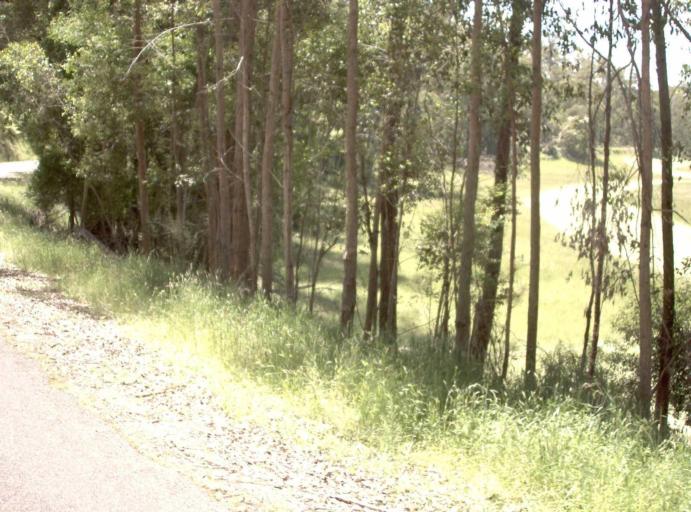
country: AU
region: New South Wales
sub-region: Bombala
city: Bombala
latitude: -37.5303
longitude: 148.9289
